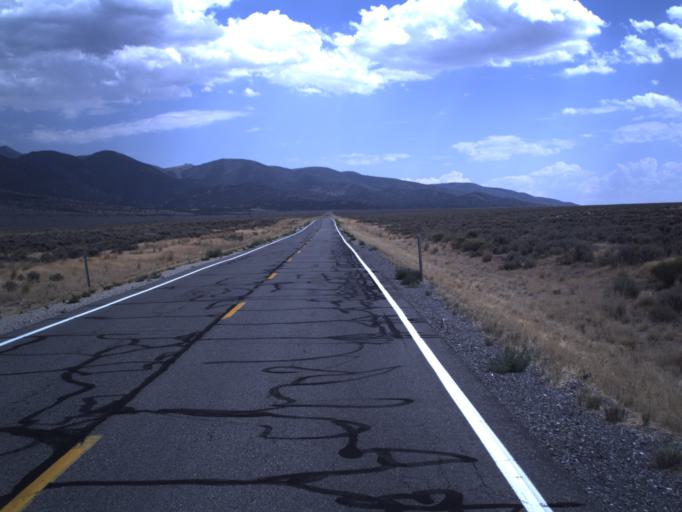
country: US
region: Utah
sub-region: Tooele County
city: Tooele
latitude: 40.3712
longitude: -112.3589
